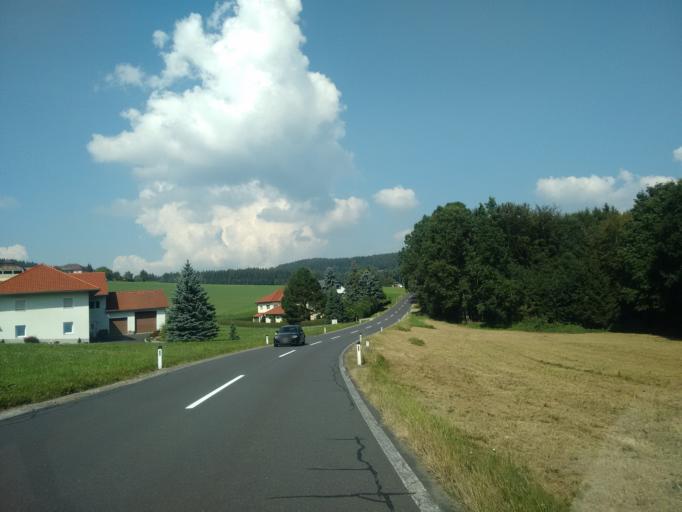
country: AT
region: Upper Austria
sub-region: Politischer Bezirk Urfahr-Umgebung
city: Altenberg bei Linz
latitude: 48.3854
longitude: 14.3431
